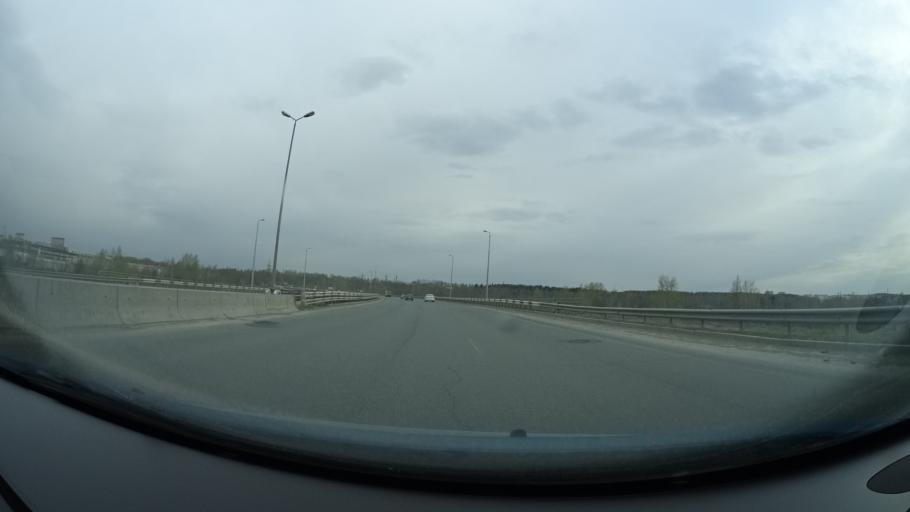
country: RU
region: Perm
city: Kondratovo
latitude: 58.0321
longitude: 56.0563
